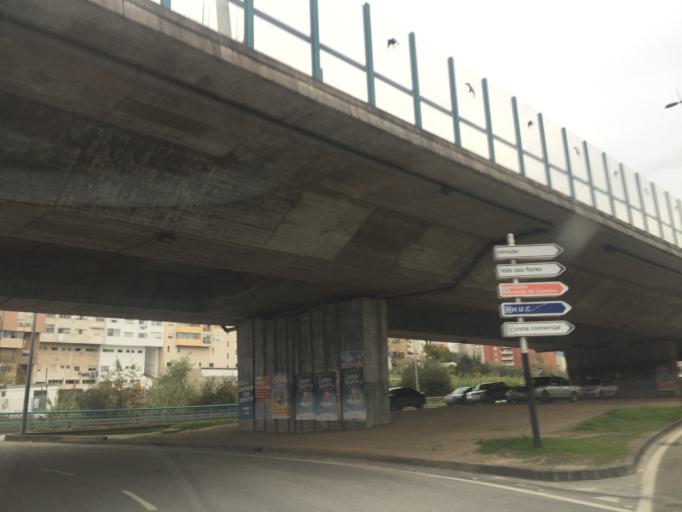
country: PT
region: Coimbra
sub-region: Coimbra
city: Coimbra
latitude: 40.1927
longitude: -8.4198
